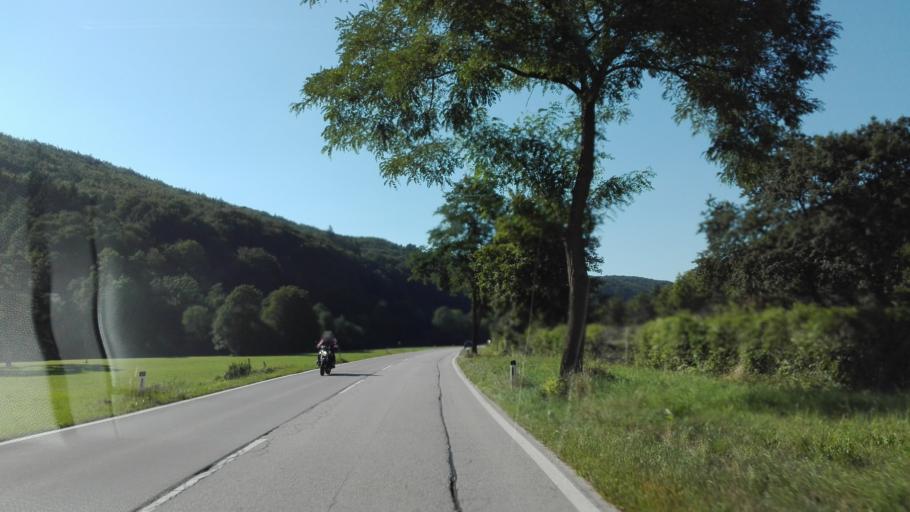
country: AT
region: Lower Austria
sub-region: Politischer Bezirk Baden
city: Alland
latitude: 48.0734
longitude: 16.0564
